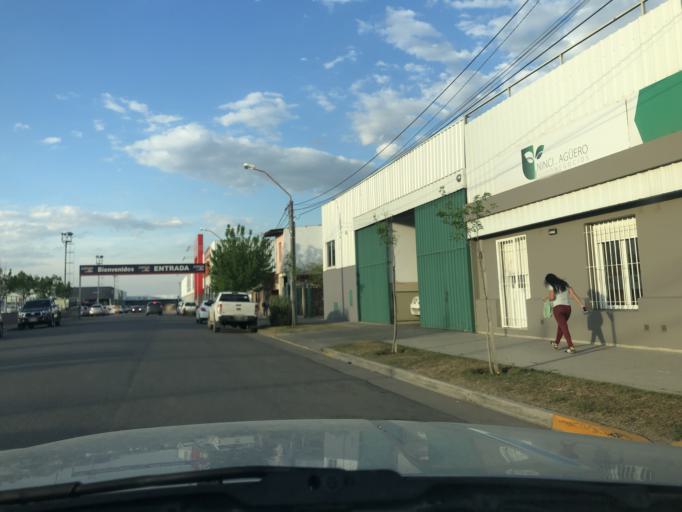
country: AR
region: Cordoba
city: Jesus Maria
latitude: -30.9776
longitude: -64.0837
